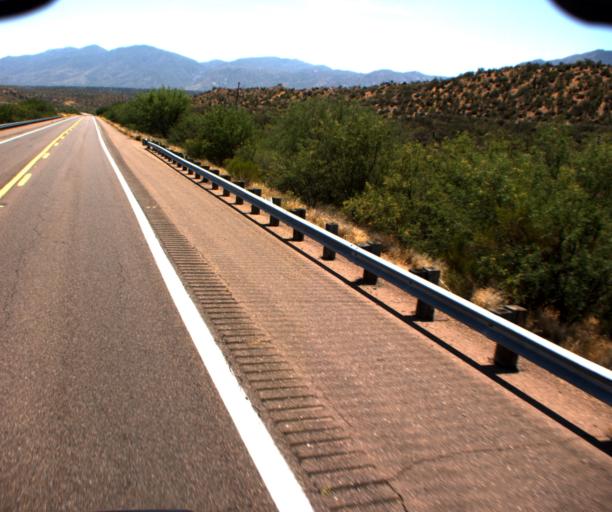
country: US
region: Arizona
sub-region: Gila County
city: Tonto Basin
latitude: 33.9311
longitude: -111.3146
